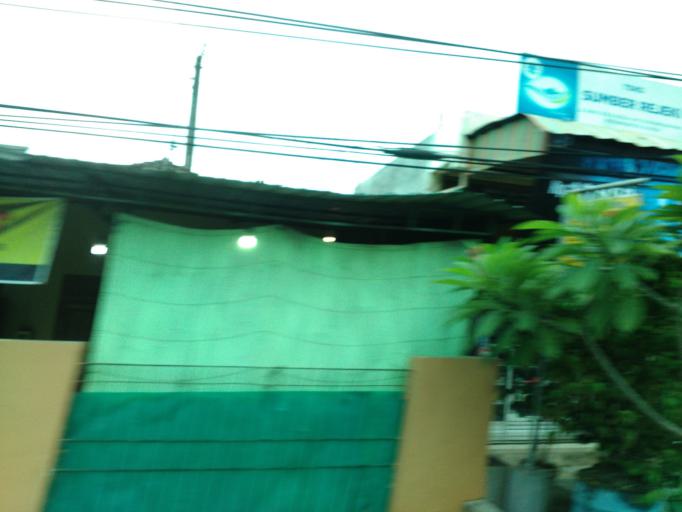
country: ID
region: Central Java
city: Gatak
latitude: -7.6045
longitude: 110.7028
